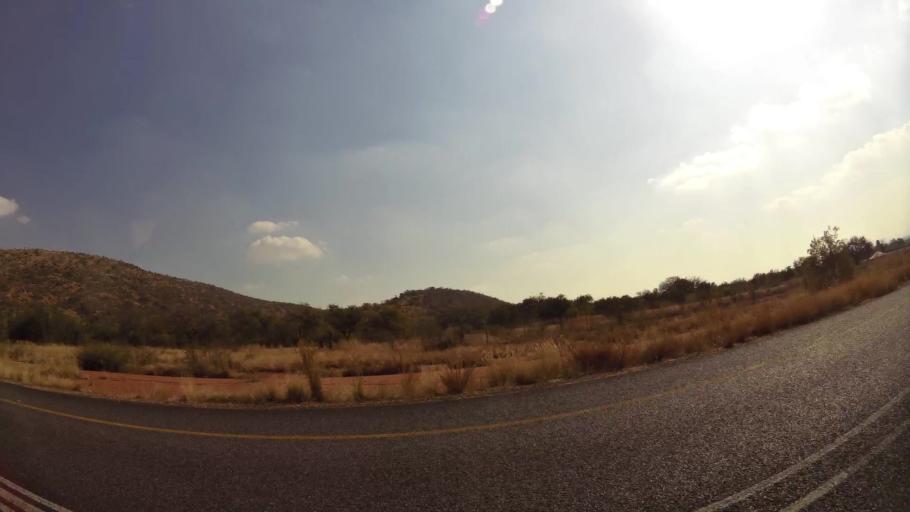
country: ZA
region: North-West
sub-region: Bojanala Platinum District Municipality
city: Rustenburg
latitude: -25.5683
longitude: 27.1410
